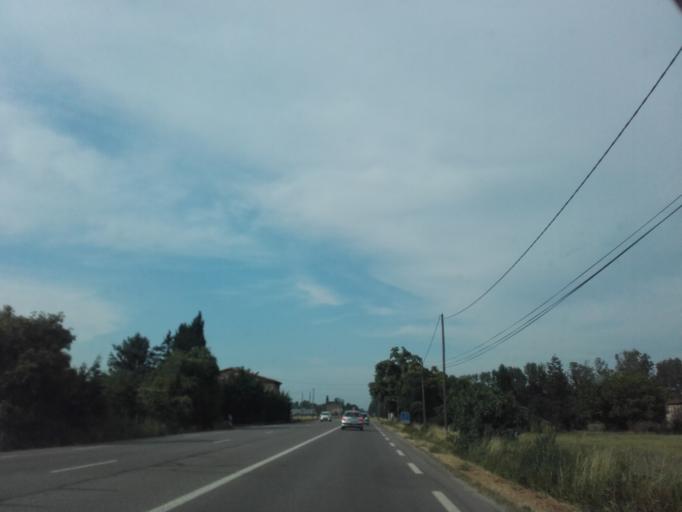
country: FR
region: Rhone-Alpes
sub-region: Departement de la Drome
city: Livron-sur-Drome
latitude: 44.7927
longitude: 4.8515
